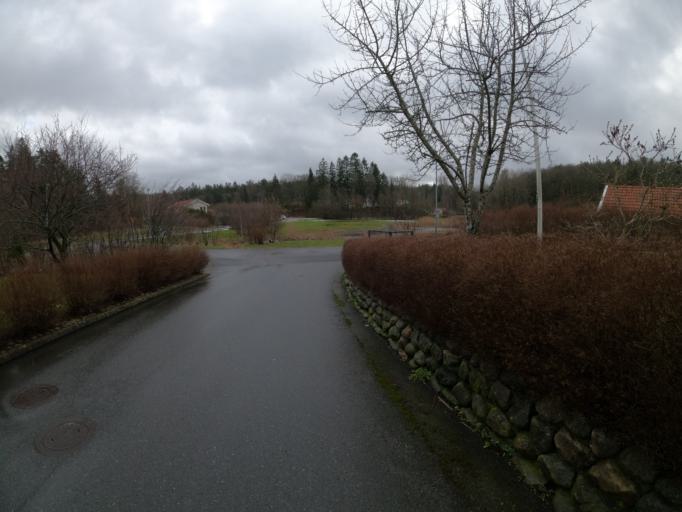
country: SE
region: Vaestra Goetaland
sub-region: Harryda Kommun
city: Molnlycke
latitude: 57.6442
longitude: 12.1054
